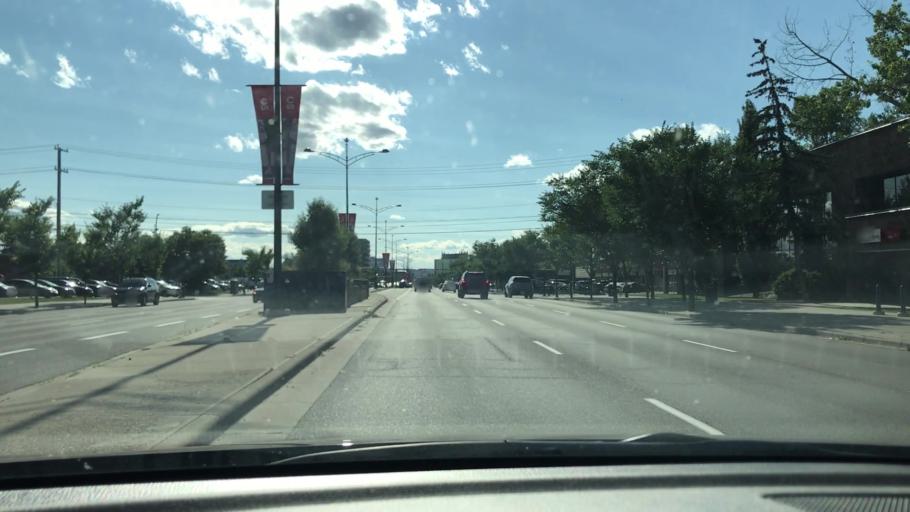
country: CA
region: Alberta
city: Calgary
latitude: 51.0670
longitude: -114.0520
